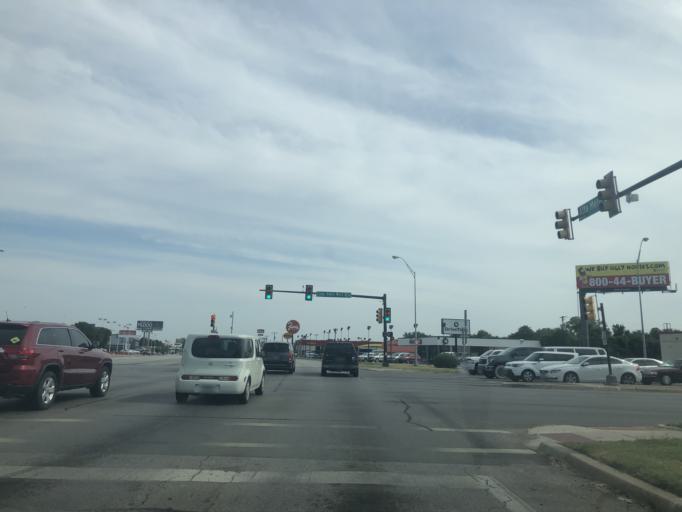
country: US
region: Texas
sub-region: Tarrant County
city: White Settlement
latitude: 32.7216
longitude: -97.4409
